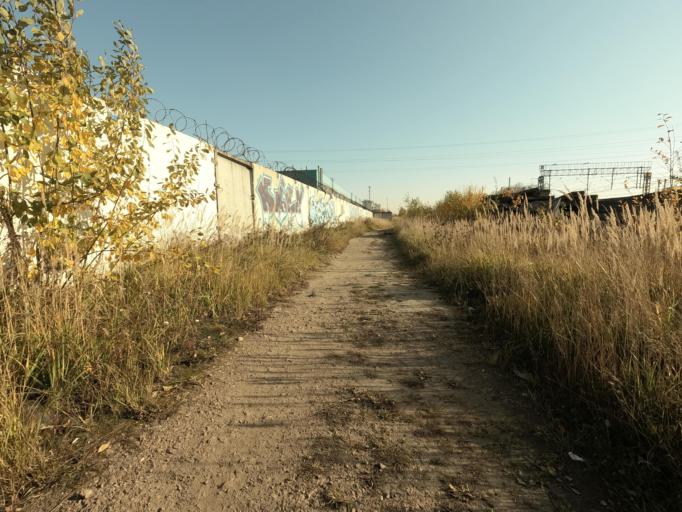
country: RU
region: St.-Petersburg
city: Obukhovo
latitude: 59.8446
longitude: 30.4665
